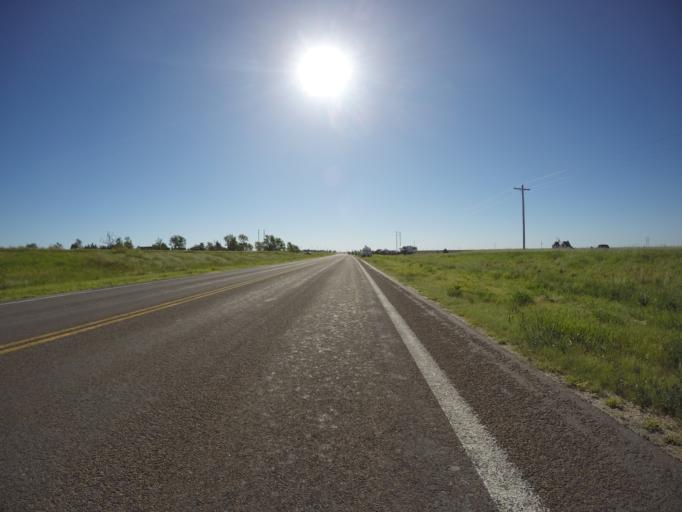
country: US
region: Kansas
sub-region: Norton County
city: Norton
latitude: 39.8276
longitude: -100.0065
